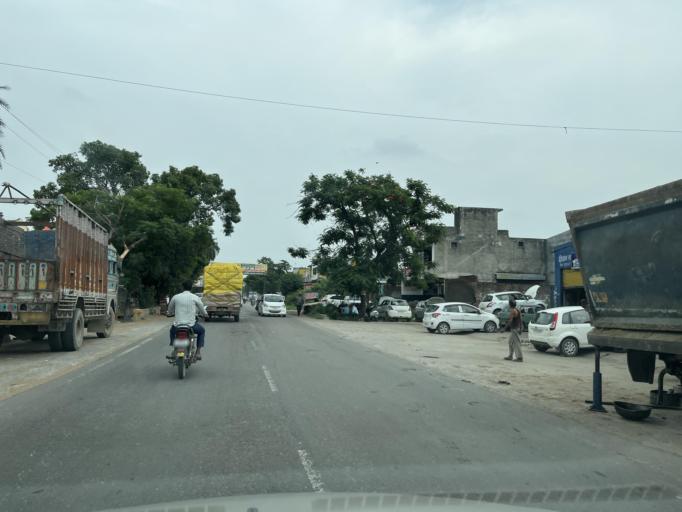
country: IN
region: Uttar Pradesh
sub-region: Rampur
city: Bilaspur
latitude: 29.0375
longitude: 79.2541
